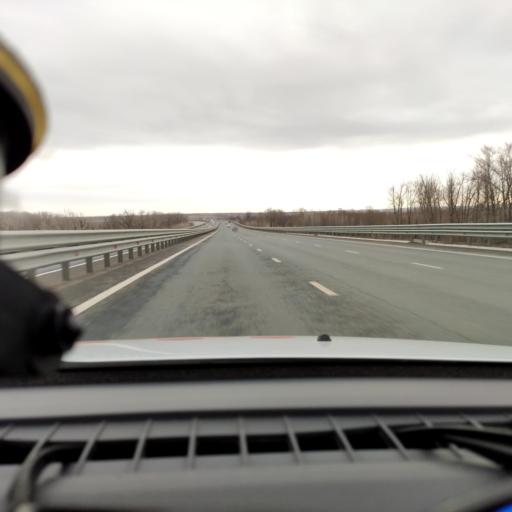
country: RU
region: Samara
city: Smyshlyayevka
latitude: 53.1747
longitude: 50.3115
